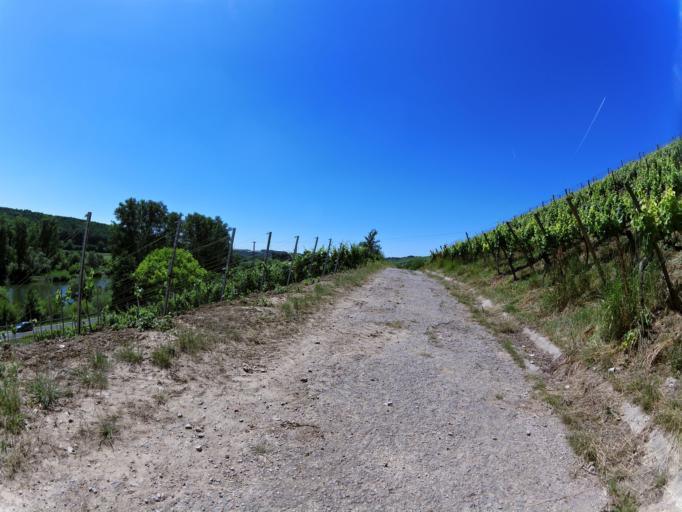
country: DE
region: Bavaria
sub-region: Regierungsbezirk Unterfranken
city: Frickenhausen
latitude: 49.6710
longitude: 10.1062
